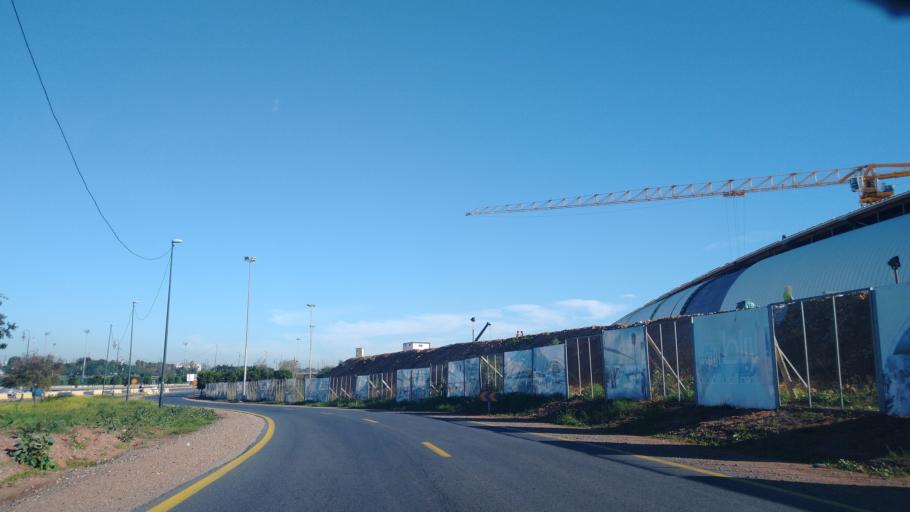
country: MA
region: Rabat-Sale-Zemmour-Zaer
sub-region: Skhirate-Temara
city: Temara
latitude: 33.9683
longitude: -6.8829
